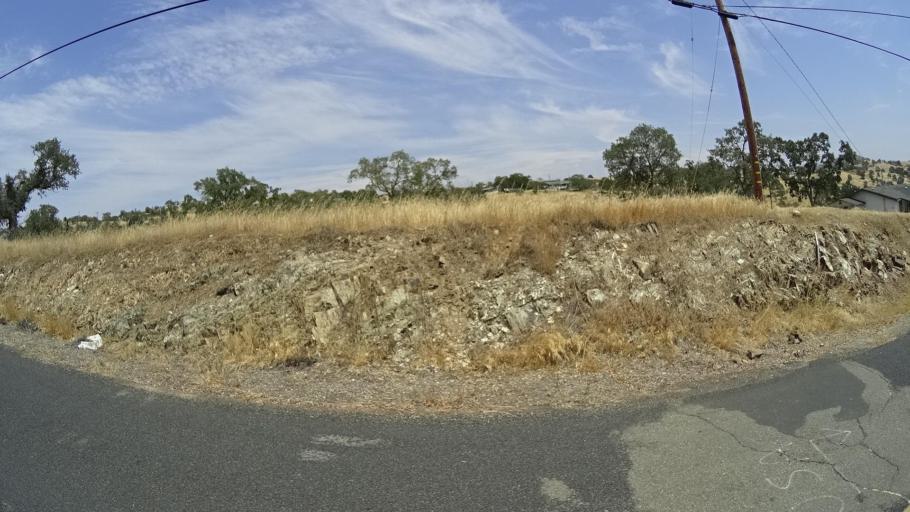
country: US
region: California
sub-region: Tuolumne County
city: Jamestown
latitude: 37.6461
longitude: -120.3511
